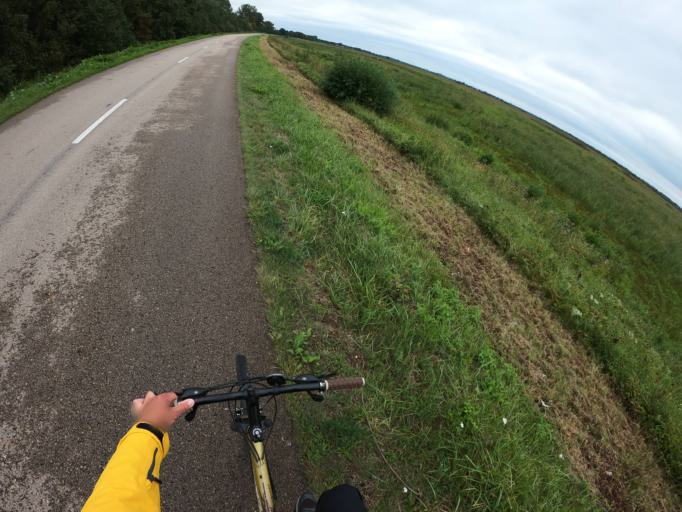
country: LT
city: Rusne
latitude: 55.3414
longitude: 21.3565
